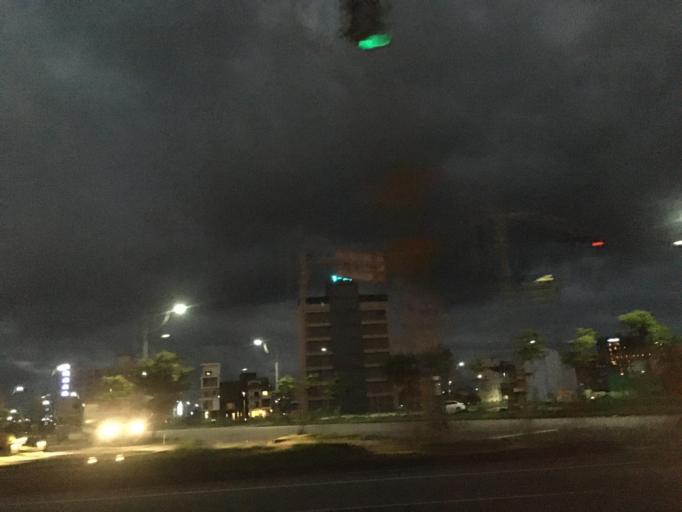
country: TW
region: Taiwan
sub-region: Yilan
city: Yilan
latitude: 24.8617
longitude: 121.8279
